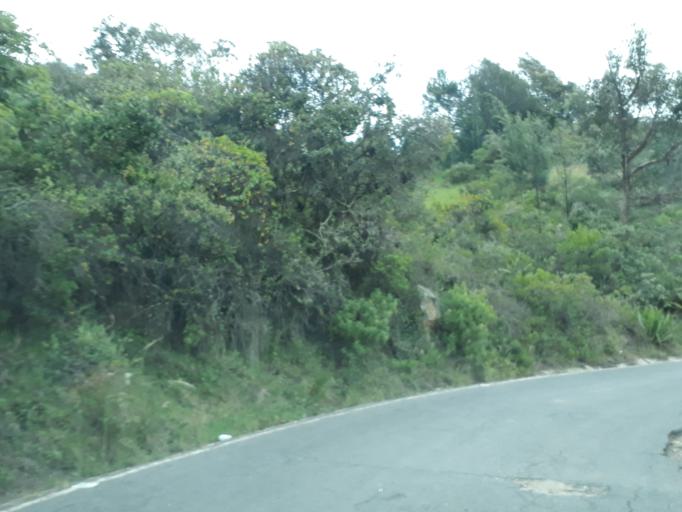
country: CO
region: Cundinamarca
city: Susa
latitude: 5.3999
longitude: -73.7727
